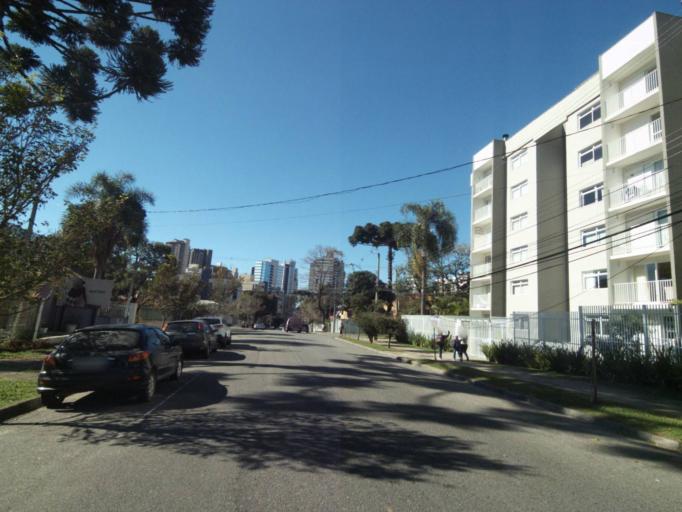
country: BR
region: Parana
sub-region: Curitiba
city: Curitiba
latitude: -25.4112
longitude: -49.2621
